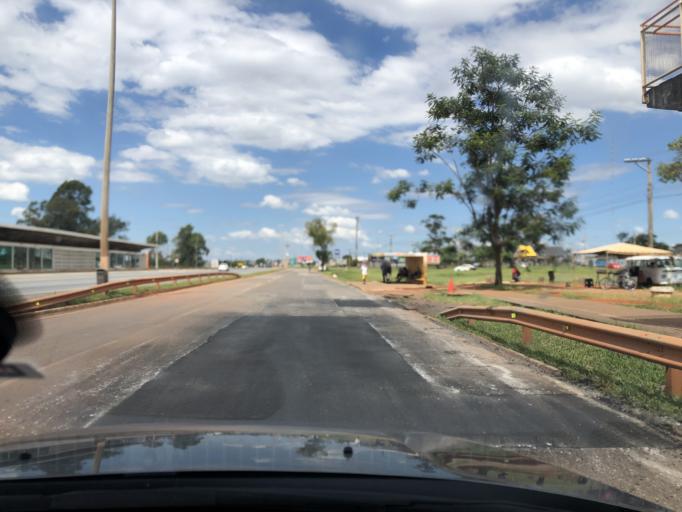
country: BR
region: Federal District
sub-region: Brasilia
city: Brasilia
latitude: -15.9921
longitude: -47.9869
